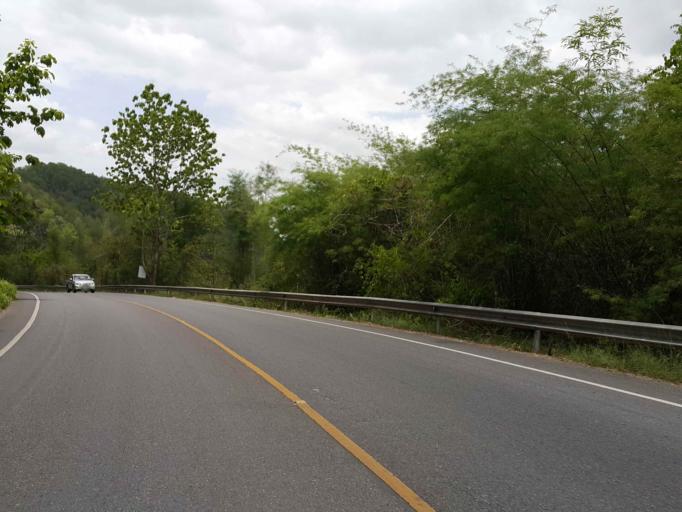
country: TH
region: Chiang Mai
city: Hang Dong
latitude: 18.7612
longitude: 98.8754
